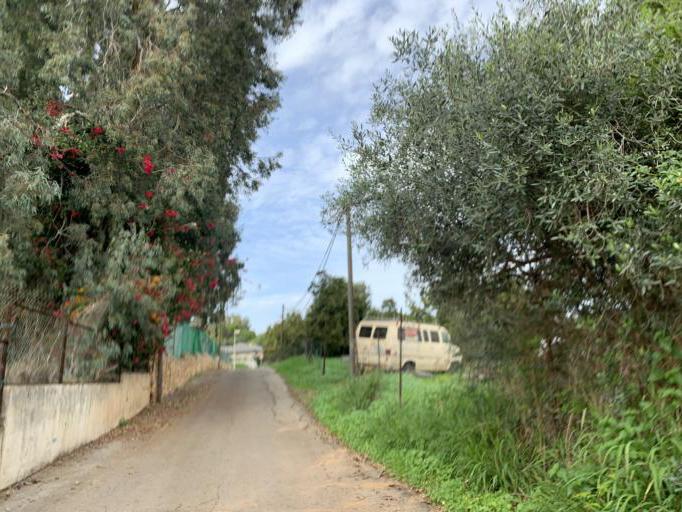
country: IL
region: Central District
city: Hod HaSharon
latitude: 32.1534
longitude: 34.9014
